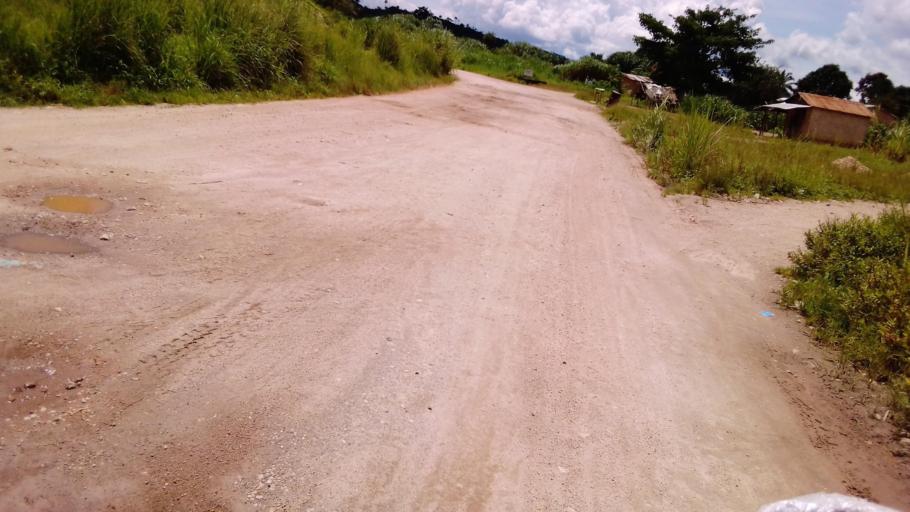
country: SL
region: Eastern Province
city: Koidu
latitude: 8.6740
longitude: -10.9951
